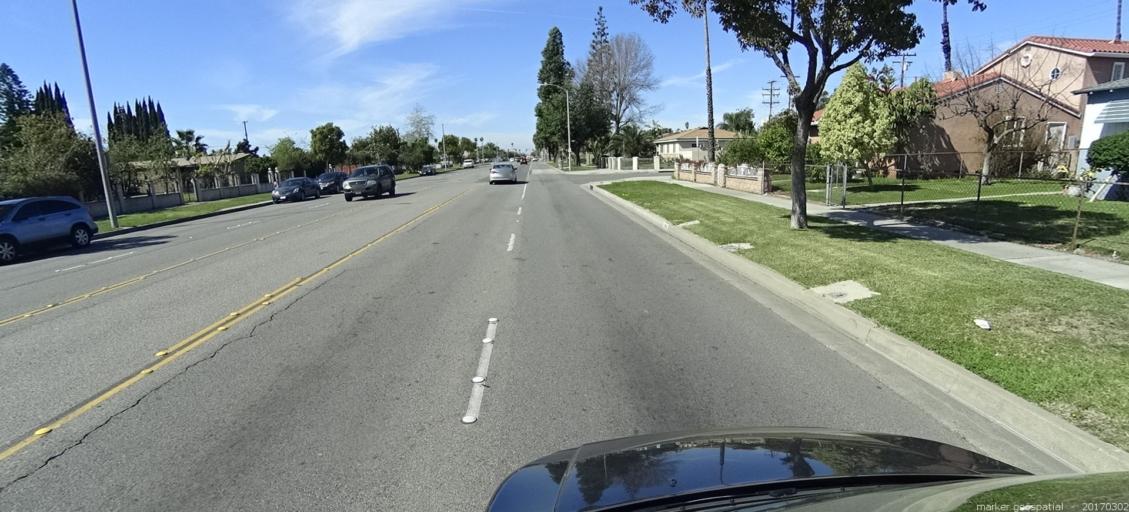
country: US
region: California
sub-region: Orange County
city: Anaheim
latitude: 33.8472
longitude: -117.9378
